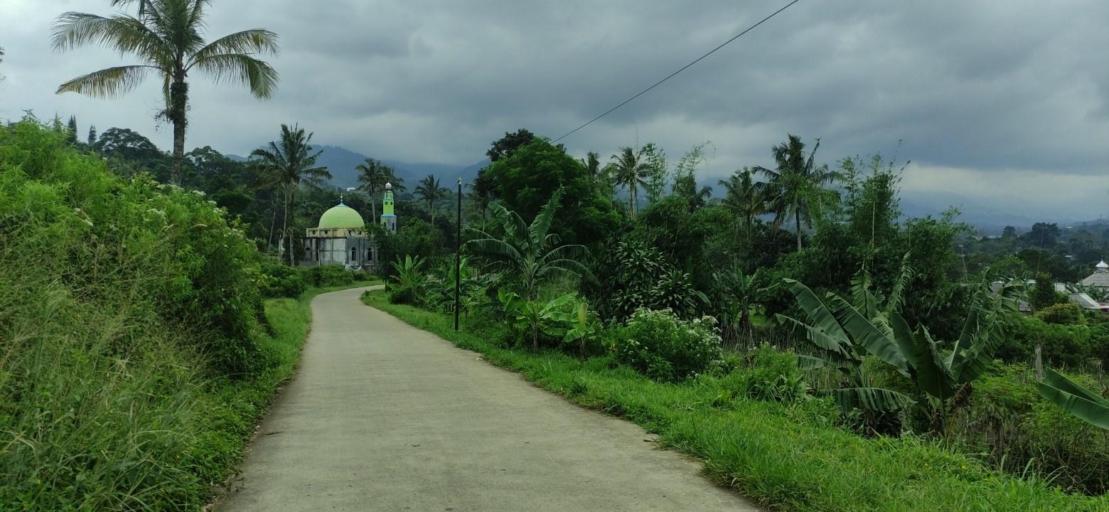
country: ID
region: West Java
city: Caringin
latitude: -6.6420
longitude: 106.8902
